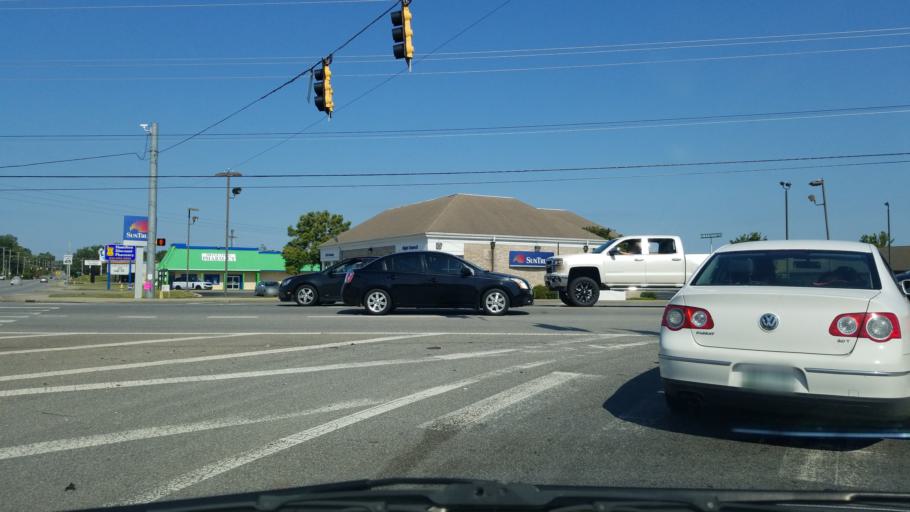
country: US
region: Tennessee
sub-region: Hamilton County
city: East Brainerd
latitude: 35.0449
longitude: -85.1620
